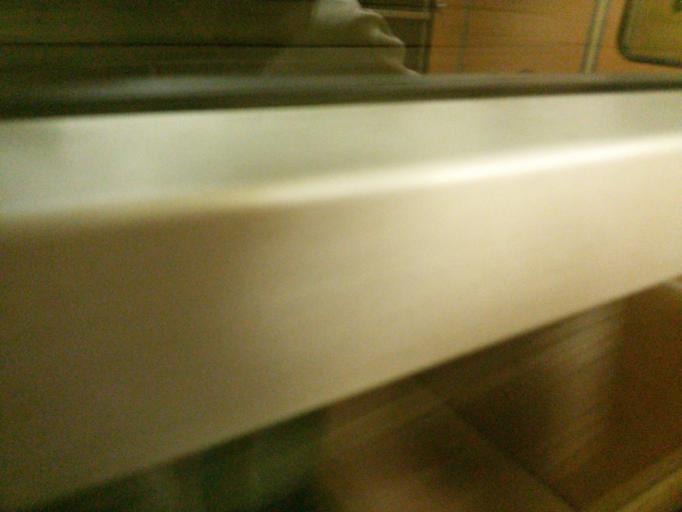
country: IT
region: Liguria
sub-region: Provincia di Genova
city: Genoa
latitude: 44.4462
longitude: 8.9441
